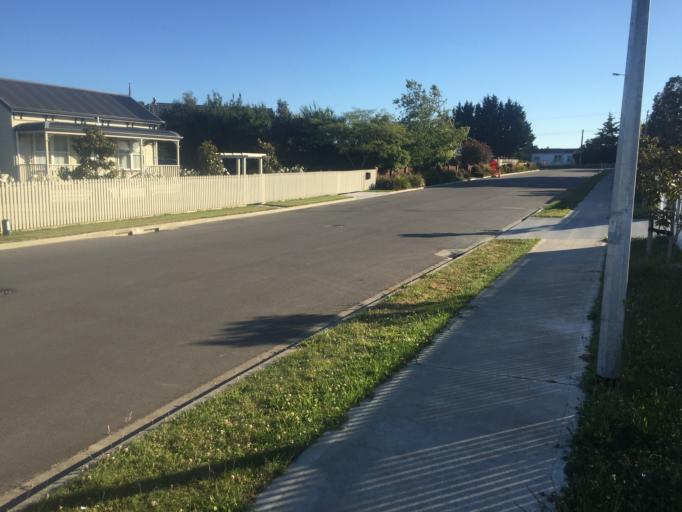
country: NZ
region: Wellington
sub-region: Masterton District
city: Masterton
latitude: -41.0834
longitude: 175.4498
